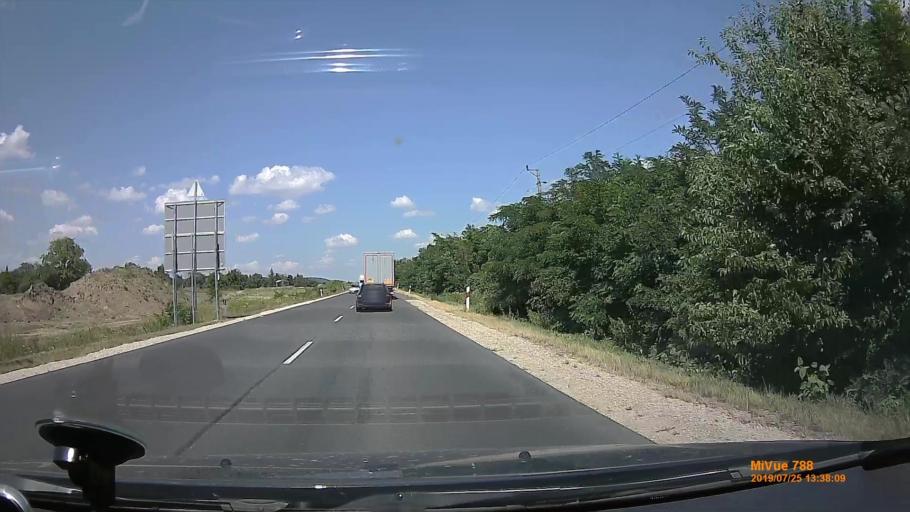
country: HU
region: Borsod-Abauj-Zemplen
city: Encs
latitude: 48.4129
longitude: 21.1766
